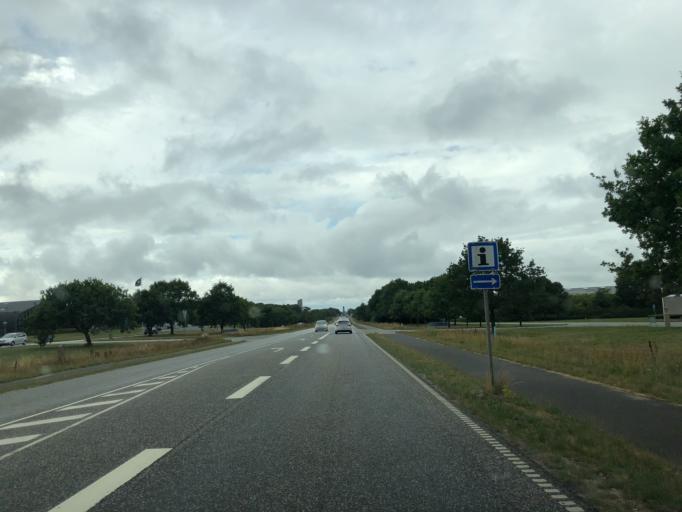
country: DK
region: Central Jutland
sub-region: Herning Kommune
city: Gjellerup Kirkeby
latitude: 56.1339
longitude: 9.0341
